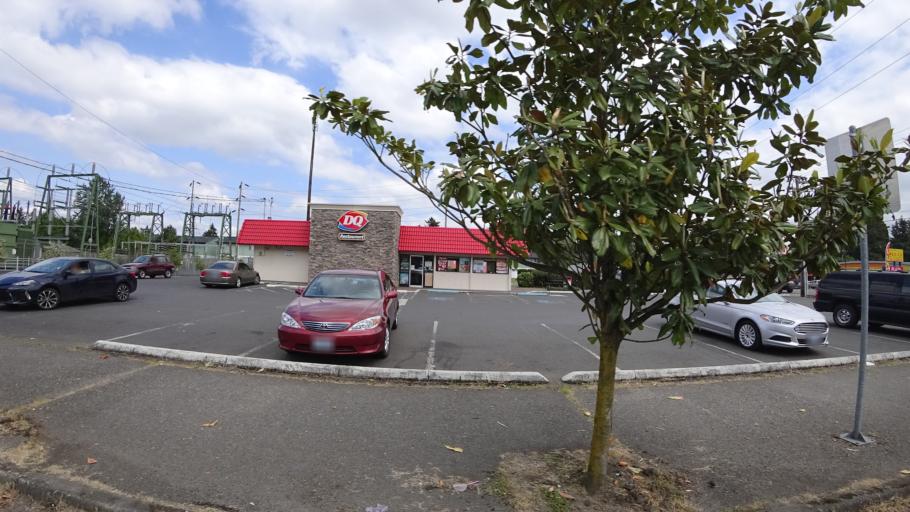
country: US
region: Oregon
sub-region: Multnomah County
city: Gresham
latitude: 45.5049
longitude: -122.4847
